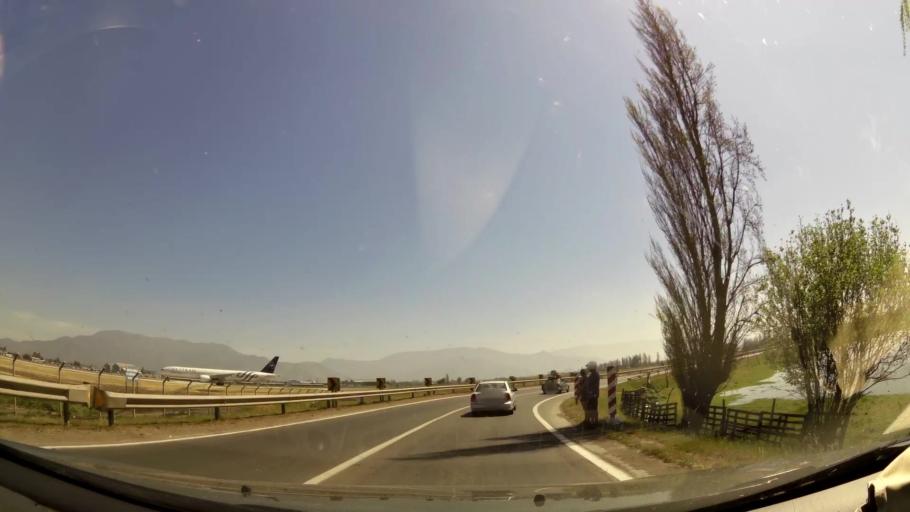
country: CL
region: Santiago Metropolitan
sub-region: Provincia de Santiago
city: Lo Prado
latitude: -33.3756
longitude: -70.7839
